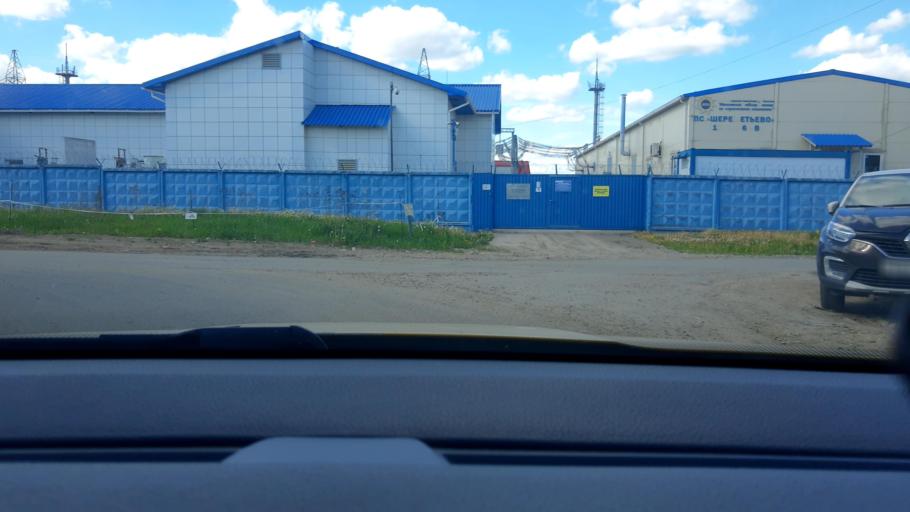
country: RU
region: Moskovskaya
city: Novopodrezkovo
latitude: 55.9845
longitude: 37.4011
